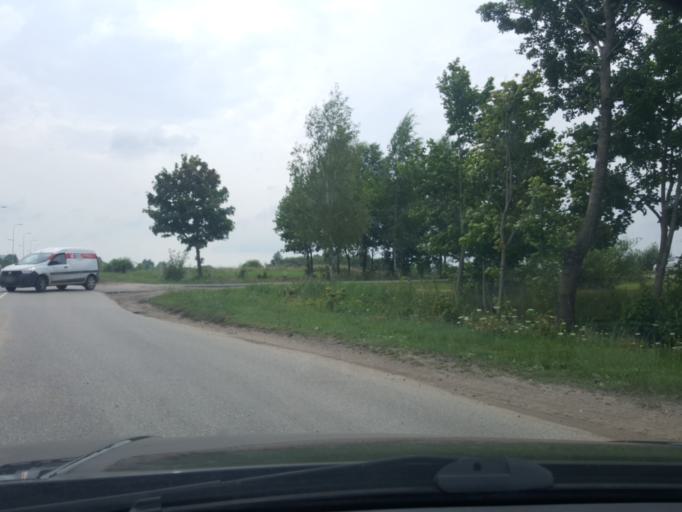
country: LT
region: Alytaus apskritis
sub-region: Alytus
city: Alytus
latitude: 54.4384
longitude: 24.0063
